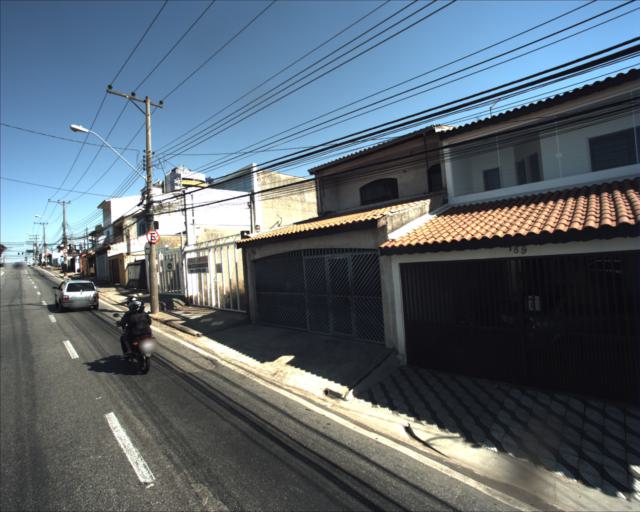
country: BR
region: Sao Paulo
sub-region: Sorocaba
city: Sorocaba
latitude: -23.4855
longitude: -47.4749
